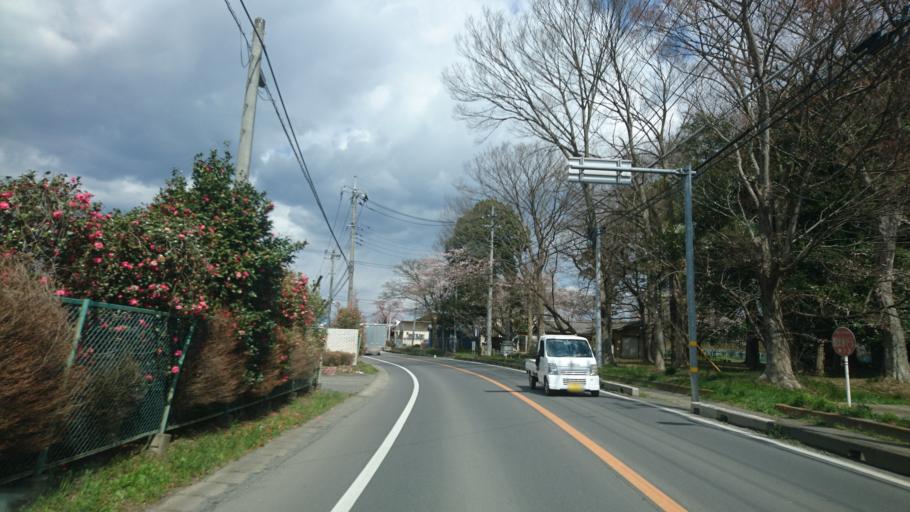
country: JP
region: Ibaraki
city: Shimodate
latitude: 36.2205
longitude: 139.9344
